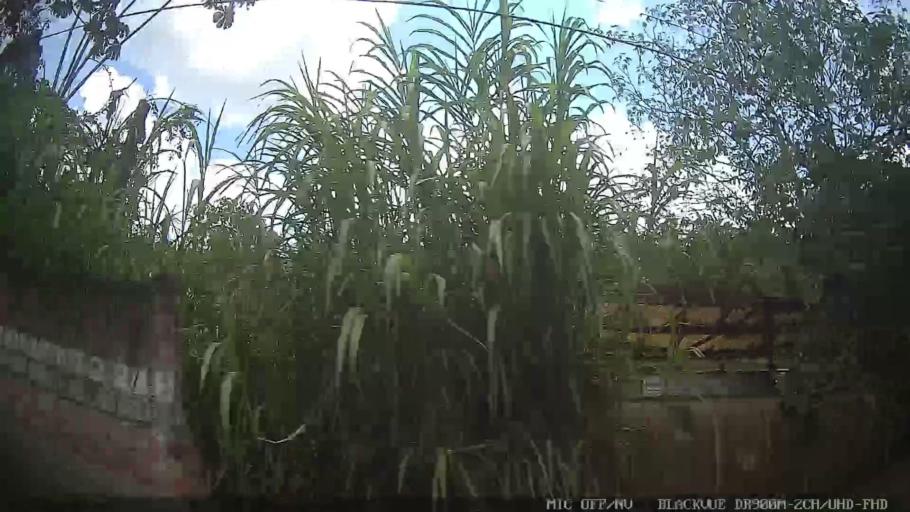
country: BR
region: Sao Paulo
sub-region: Jarinu
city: Jarinu
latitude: -23.0727
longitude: -46.6432
